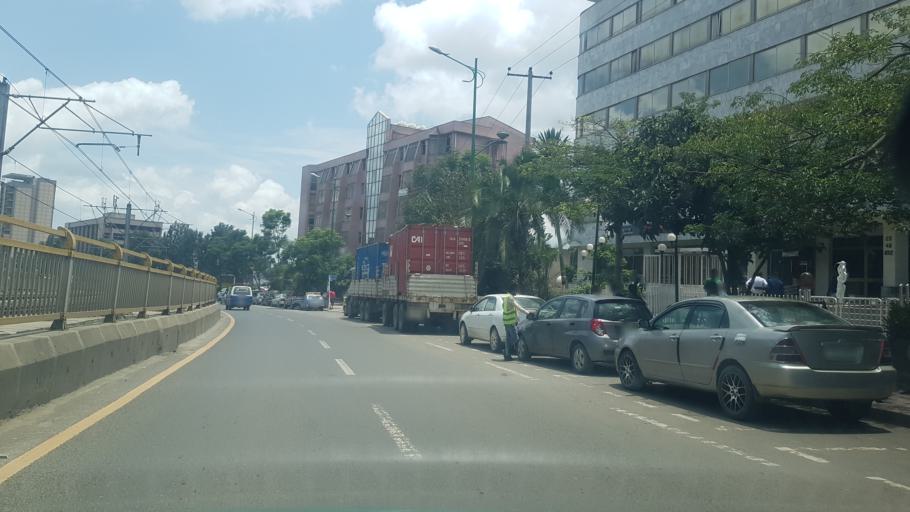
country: ET
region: Adis Abeba
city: Addis Ababa
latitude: 8.9927
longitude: 38.7591
